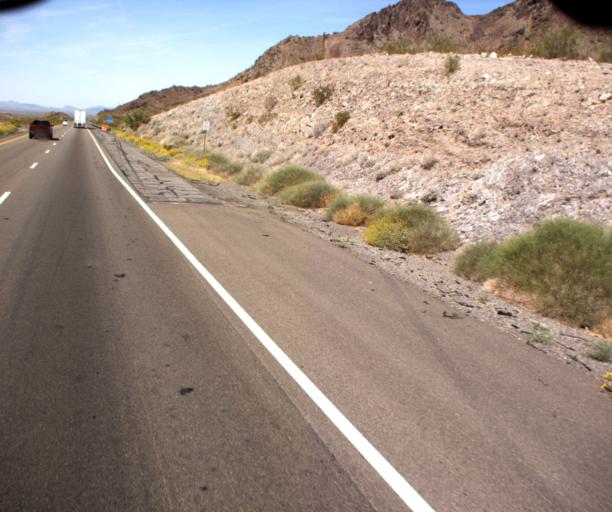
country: US
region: Arizona
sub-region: La Paz County
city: Salome
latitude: 33.6108
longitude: -113.6296
